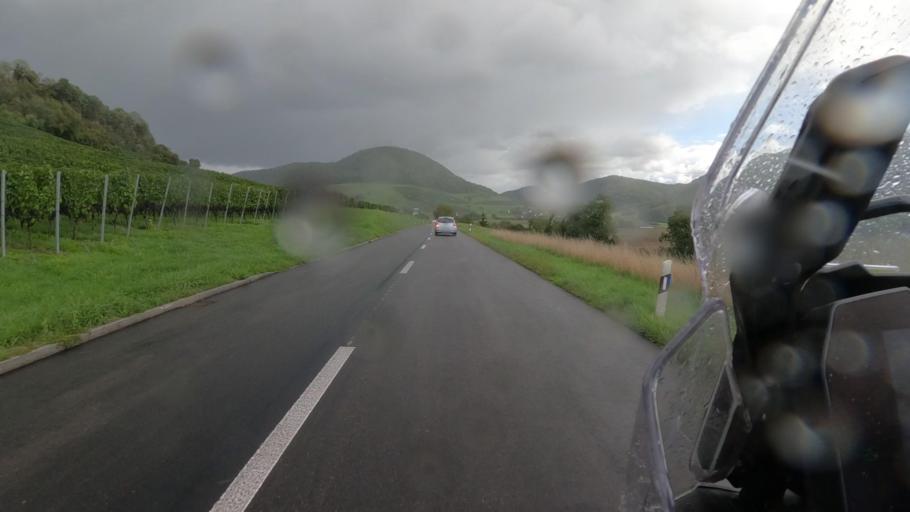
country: CH
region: Schaffhausen
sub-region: Bezirk Unterklettgau
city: Wilchingen
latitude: 47.6627
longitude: 8.4719
